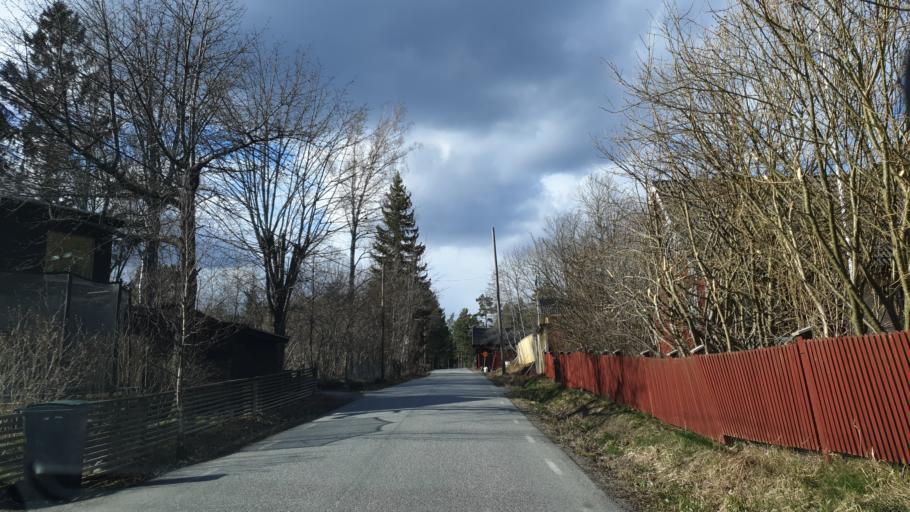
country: SE
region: Stockholm
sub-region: Tyreso Kommun
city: Brevik
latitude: 59.2450
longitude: 18.4429
